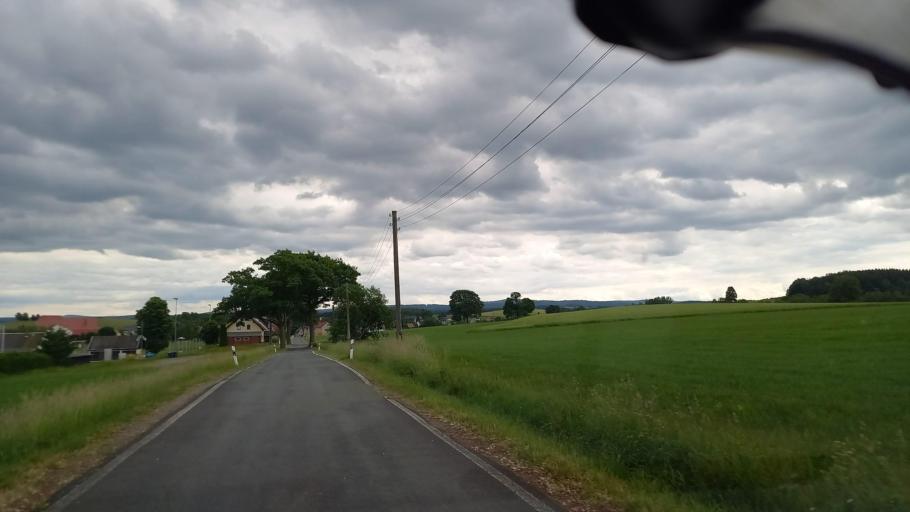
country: DE
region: Saxony
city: Waldkirchen
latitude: 50.6153
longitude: 12.4195
